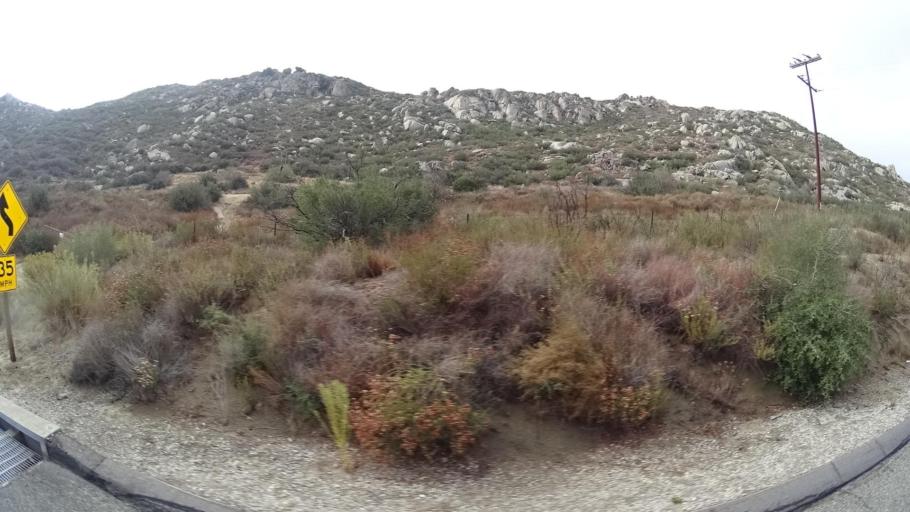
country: MX
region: Baja California
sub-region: Tecate
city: Hacienda Tecate
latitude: 32.5961
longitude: -116.5461
